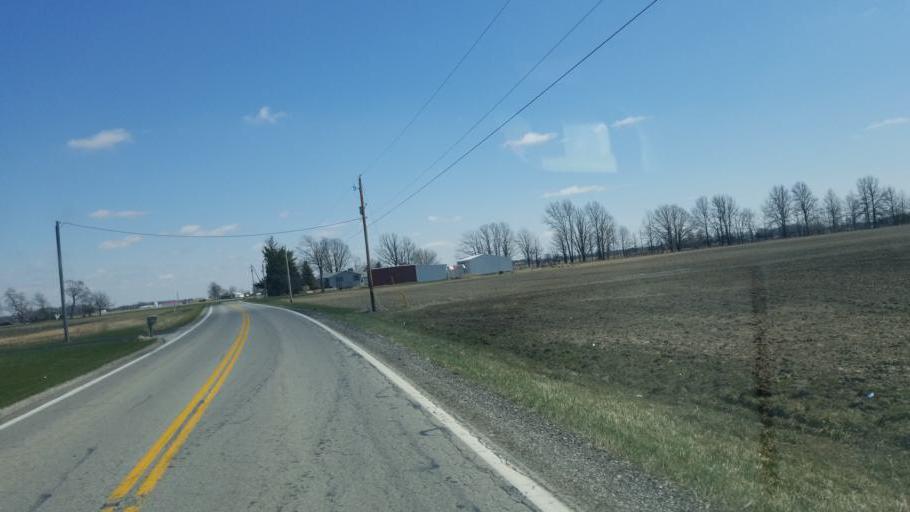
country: US
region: Ohio
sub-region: Marion County
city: Prospect
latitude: 40.4514
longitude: -83.1194
